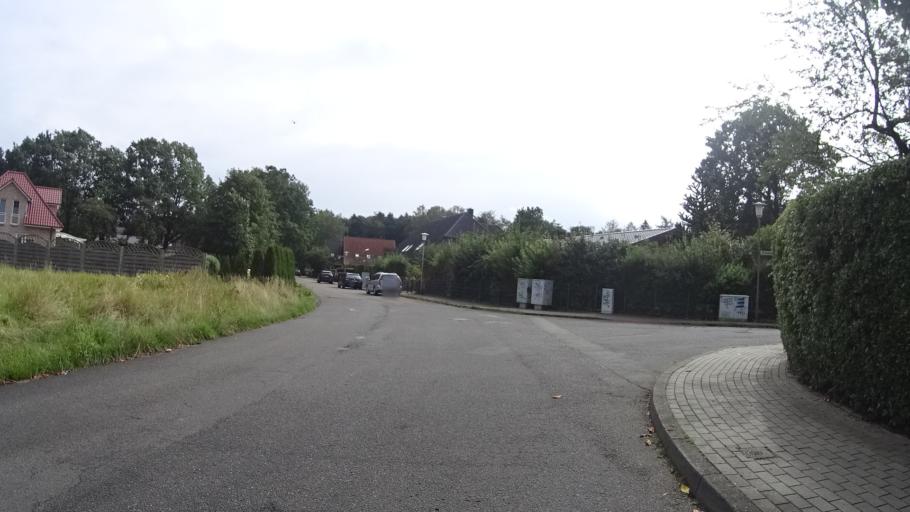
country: DE
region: Schleswig-Holstein
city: Henstedt-Ulzburg
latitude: 53.7614
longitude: 9.9933
